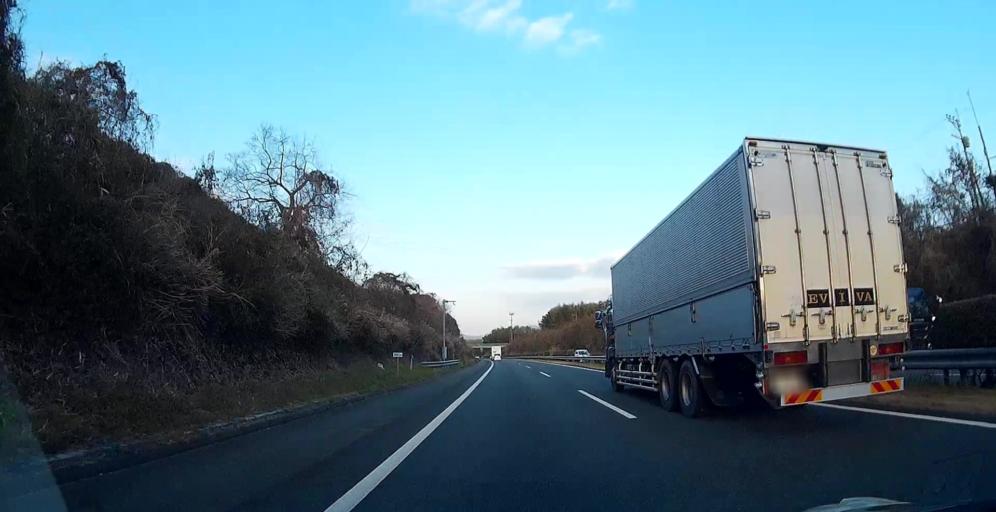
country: JP
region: Kumamoto
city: Uto
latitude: 32.6800
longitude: 130.7290
